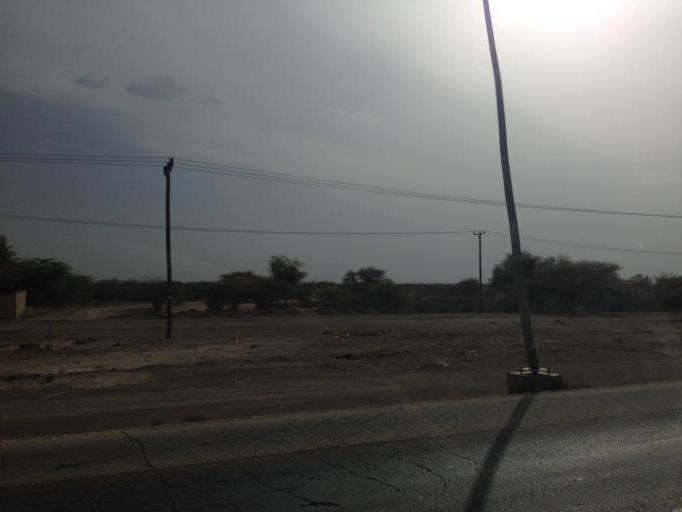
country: OM
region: Ash Sharqiyah
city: Al Qabil
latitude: 22.5952
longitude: 58.6754
